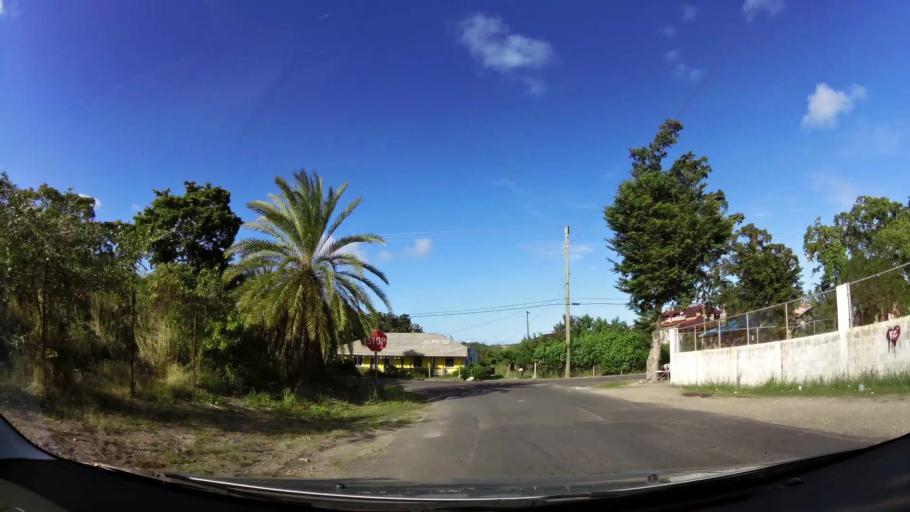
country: AG
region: Saint George
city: Piggotts
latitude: 17.1094
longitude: -61.7993
